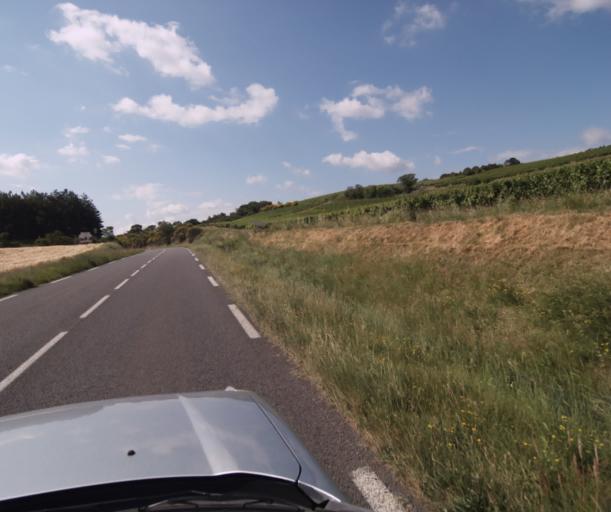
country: FR
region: Languedoc-Roussillon
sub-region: Departement de l'Aude
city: Limoux
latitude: 43.0752
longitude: 2.1971
